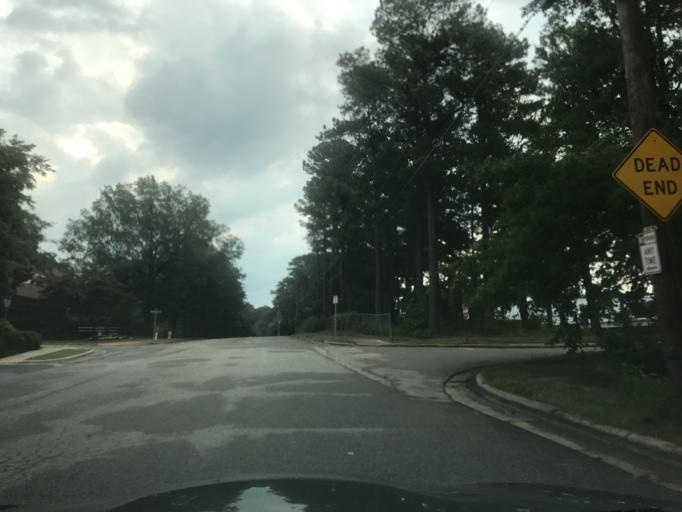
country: US
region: North Carolina
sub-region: Wake County
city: West Raleigh
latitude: 35.8440
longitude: -78.6431
